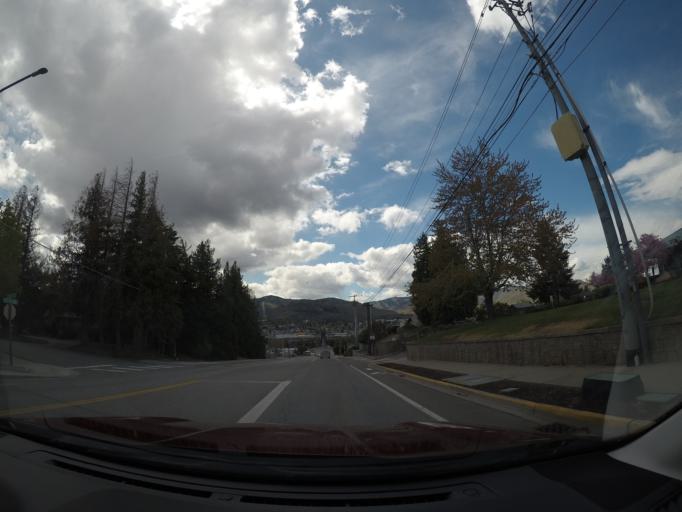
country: US
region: Washington
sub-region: Douglas County
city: East Wenatchee
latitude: 47.4168
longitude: -120.2894
